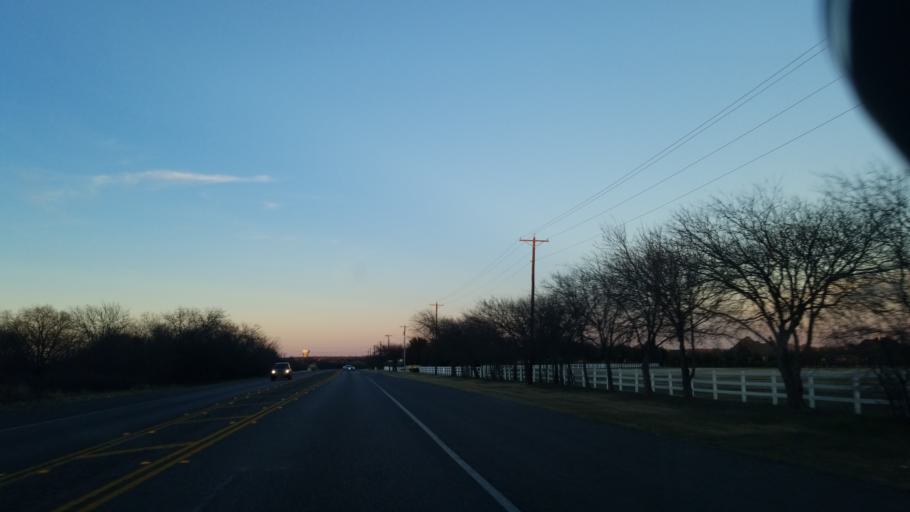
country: US
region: Texas
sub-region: Denton County
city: Argyle
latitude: 33.1561
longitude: -97.1638
